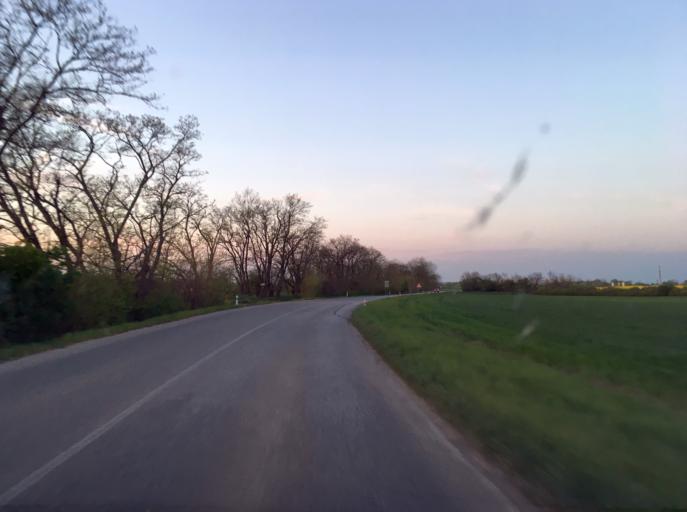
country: SK
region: Nitriansky
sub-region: Okres Nove Zamky
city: Nove Zamky
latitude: 47.9623
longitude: 18.1477
